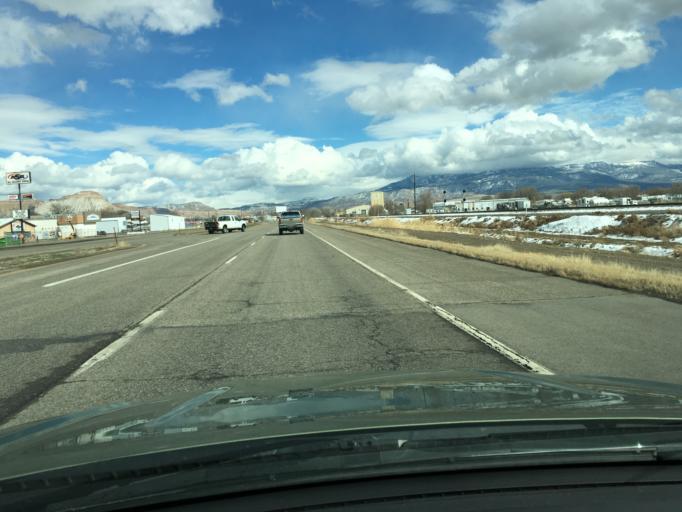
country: US
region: Colorado
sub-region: Mesa County
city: Fruitvale
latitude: 39.0751
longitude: -108.5052
